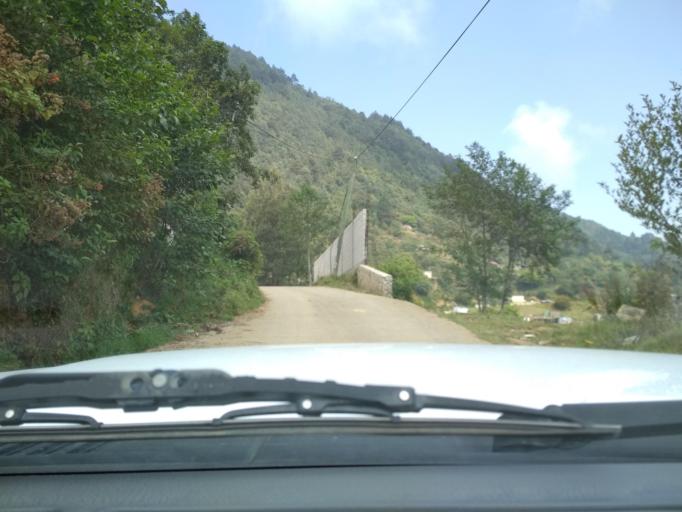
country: MX
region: Veracruz
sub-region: Camerino Z. Mendoza
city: Necoxtla
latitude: 18.7659
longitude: -97.1524
